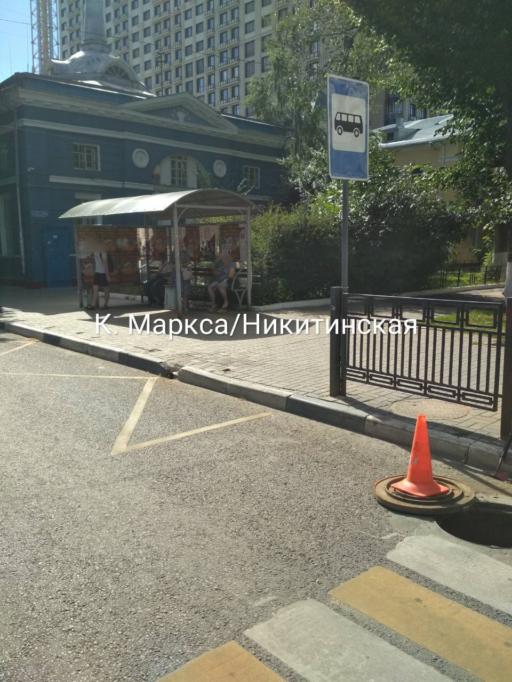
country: RU
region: Voronezj
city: Voronezh
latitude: 51.6676
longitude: 39.2010
